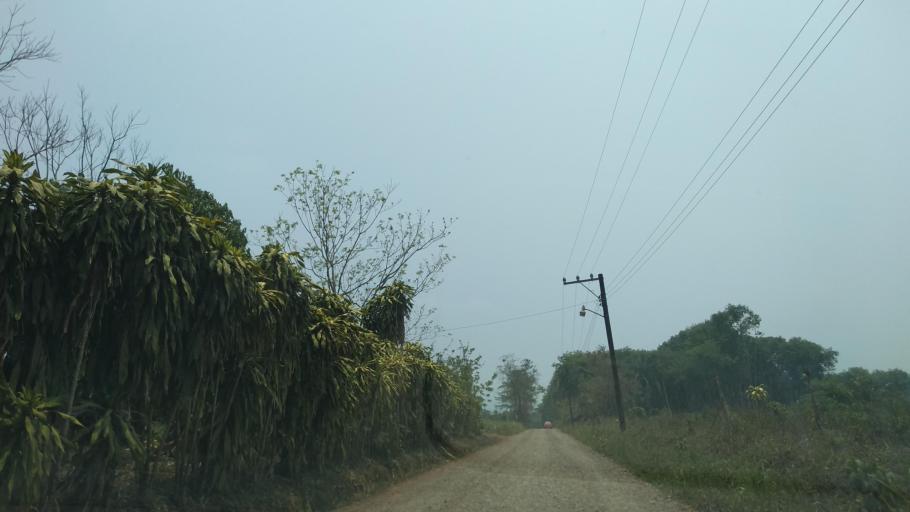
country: MX
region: Veracruz
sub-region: Tezonapa
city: Laguna Chica (Pueblo Nuevo)
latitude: 18.4992
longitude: -96.7748
